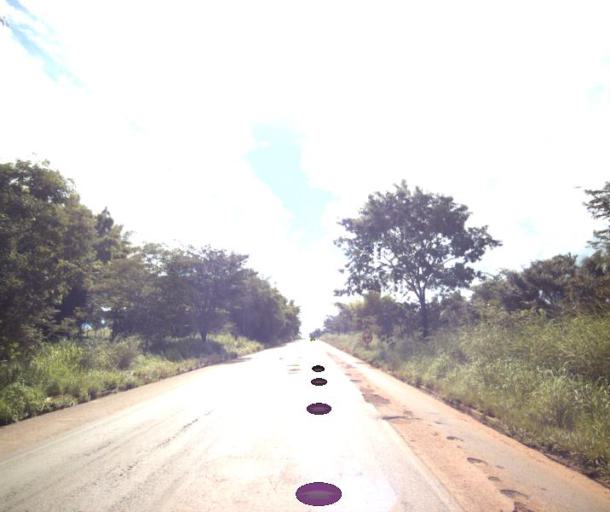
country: BR
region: Goias
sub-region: Petrolina De Goias
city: Petrolina de Goias
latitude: -15.9862
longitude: -49.1560
